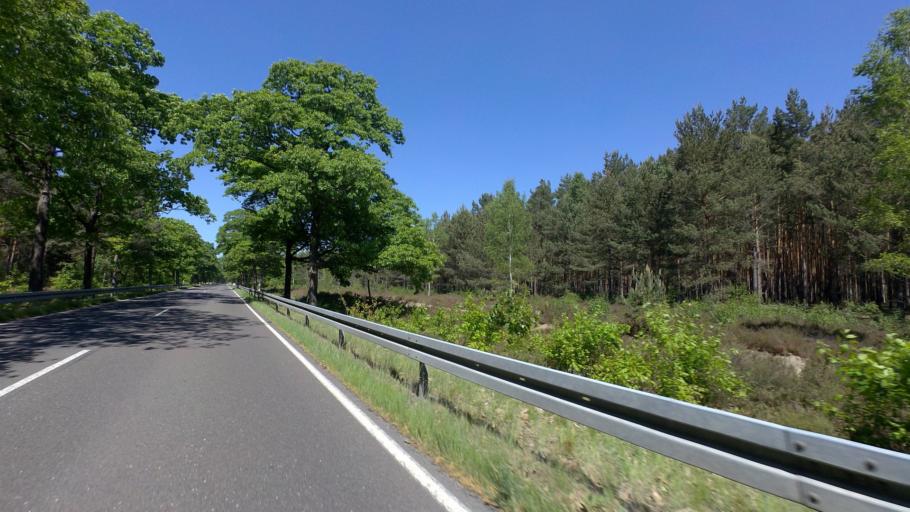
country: DE
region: Brandenburg
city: Drachhausen
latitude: 51.9191
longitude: 14.3491
